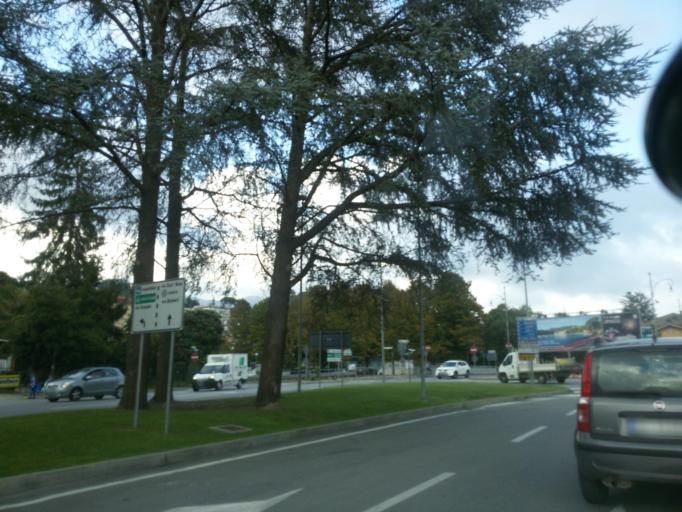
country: IT
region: Liguria
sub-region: Provincia di Genova
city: Rapallo
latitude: 44.3556
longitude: 9.2102
